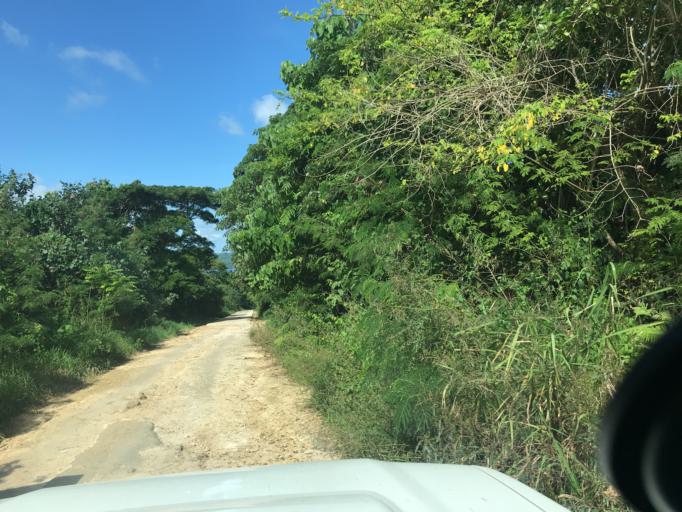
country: VU
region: Sanma
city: Luganville
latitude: -15.5251
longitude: 167.1489
